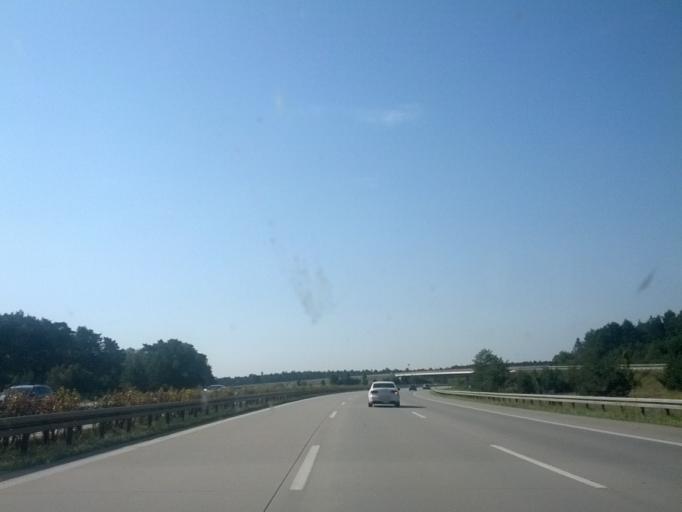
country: DE
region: Brandenburg
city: Erkner
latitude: 52.3300
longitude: 13.7508
